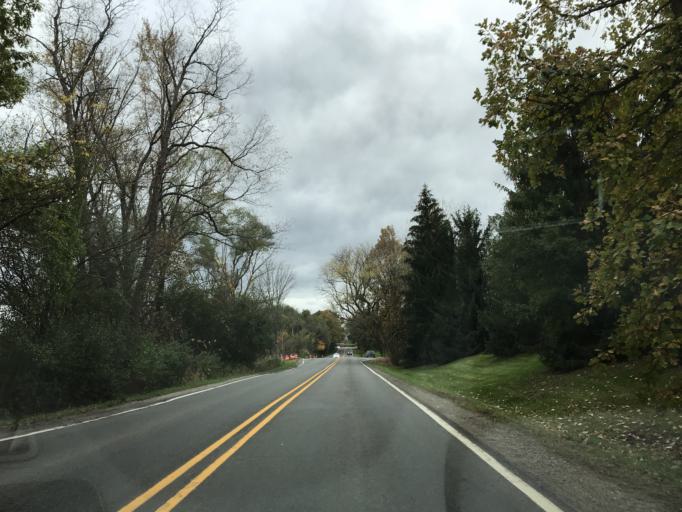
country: US
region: Michigan
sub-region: Washtenaw County
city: Ann Arbor
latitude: 42.2795
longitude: -83.6715
